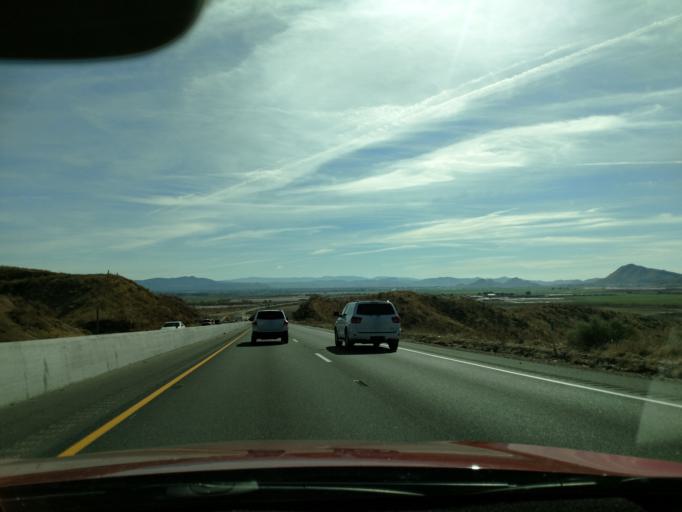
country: US
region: California
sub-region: Riverside County
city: Beaumont
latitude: 33.8544
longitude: -117.0086
